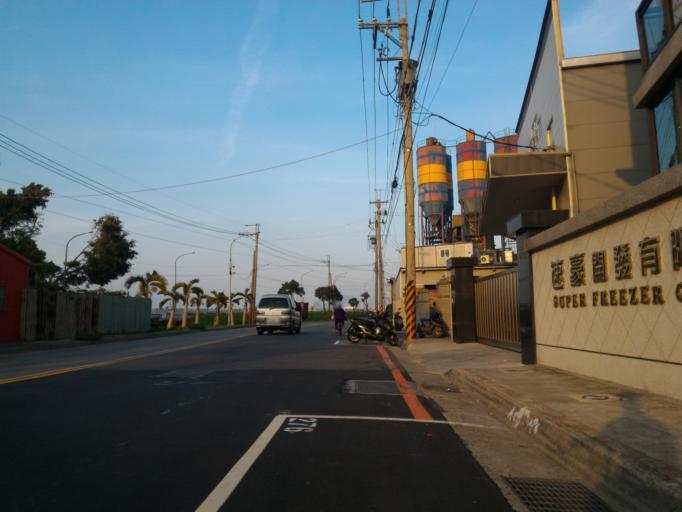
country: TW
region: Taipei
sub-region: Taipei
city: Banqiao
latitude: 24.9716
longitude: 121.4151
